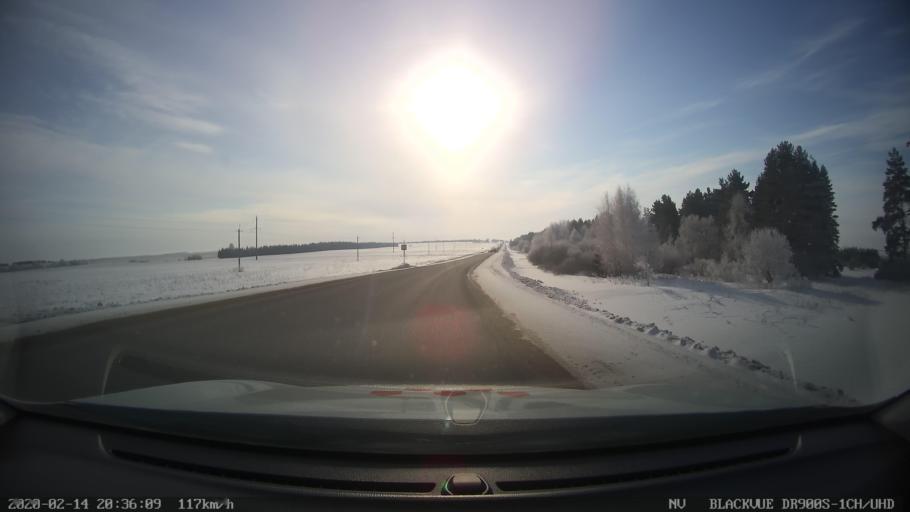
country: RU
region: Tatarstan
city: Kuybyshevskiy Zaton
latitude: 55.3734
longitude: 48.9959
